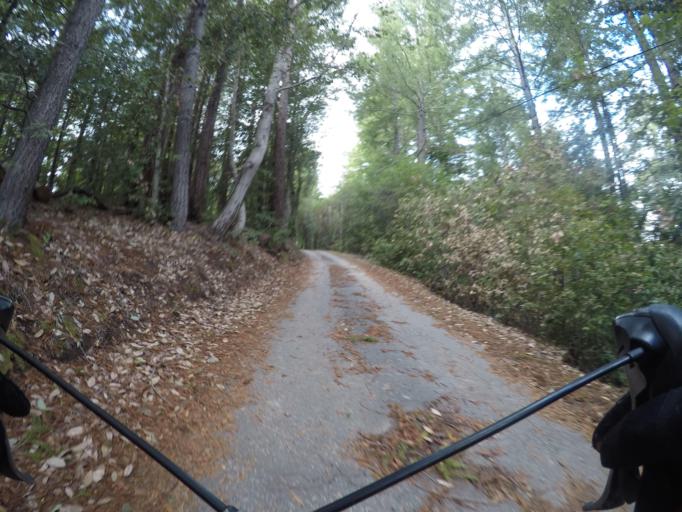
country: US
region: California
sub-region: Santa Cruz County
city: Brookdale
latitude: 37.1109
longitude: -122.0937
